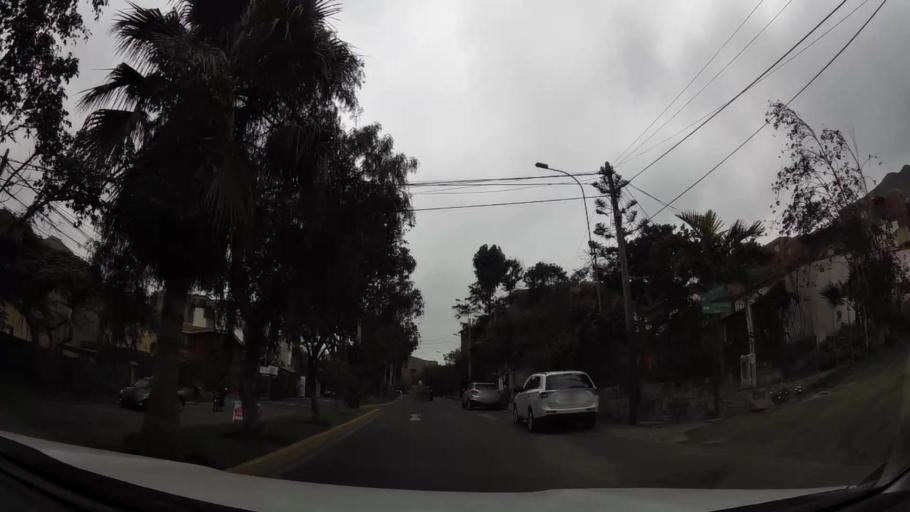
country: PE
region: Lima
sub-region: Lima
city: La Molina
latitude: -12.1078
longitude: -76.9594
